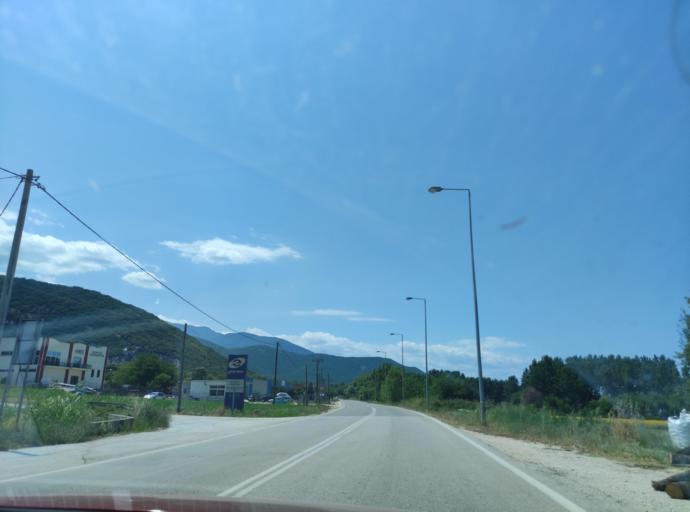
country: GR
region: East Macedonia and Thrace
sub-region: Nomos Kavalas
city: Palaiochori
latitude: 40.9511
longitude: 24.2047
